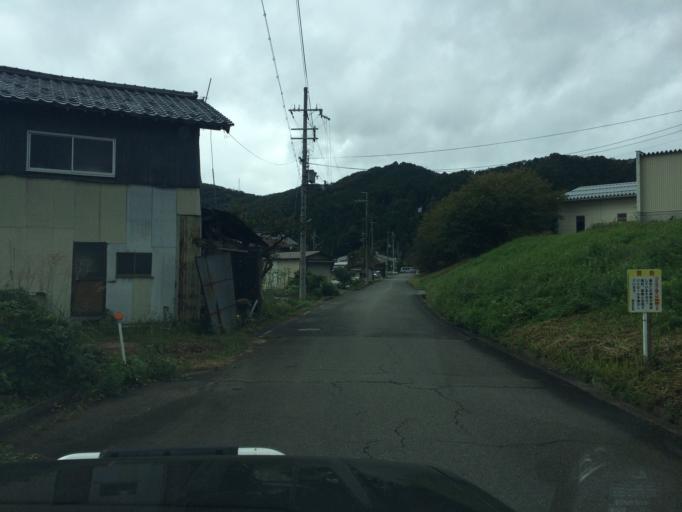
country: JP
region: Hyogo
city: Toyooka
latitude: 35.4979
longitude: 134.8068
